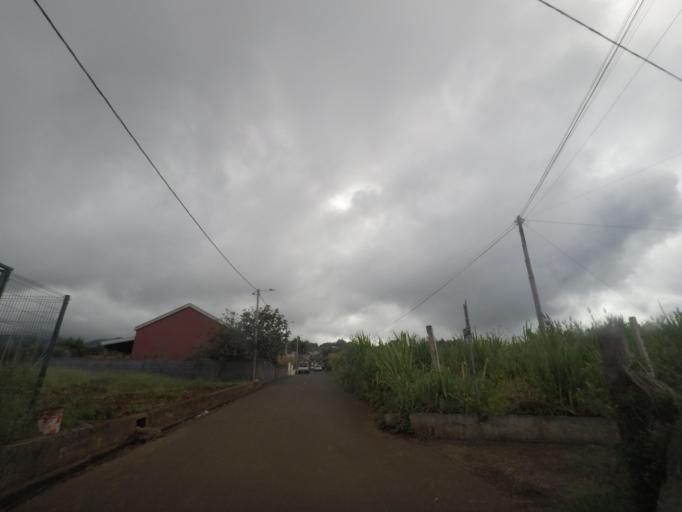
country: PT
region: Madeira
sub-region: Santana
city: Santana
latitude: 32.8338
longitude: -16.9066
